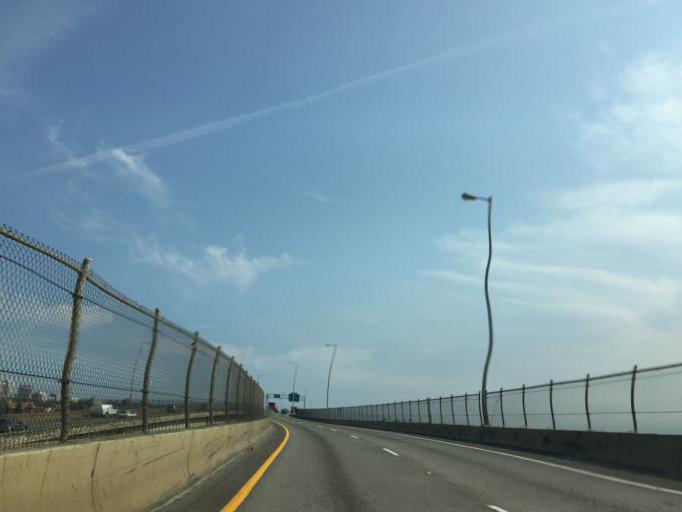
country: US
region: Oregon
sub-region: Multnomah County
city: Portland
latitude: 45.5054
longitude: -122.6729
